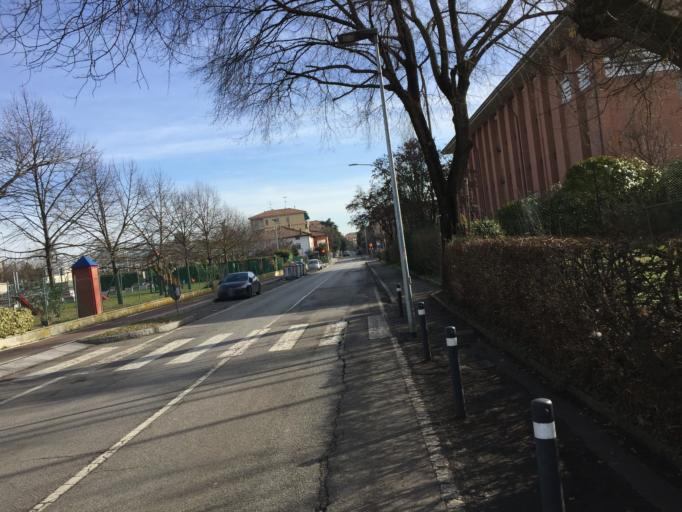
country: IT
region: Emilia-Romagna
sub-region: Provincia di Bologna
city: Calderara di Reno
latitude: 44.5229
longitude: 11.2716
